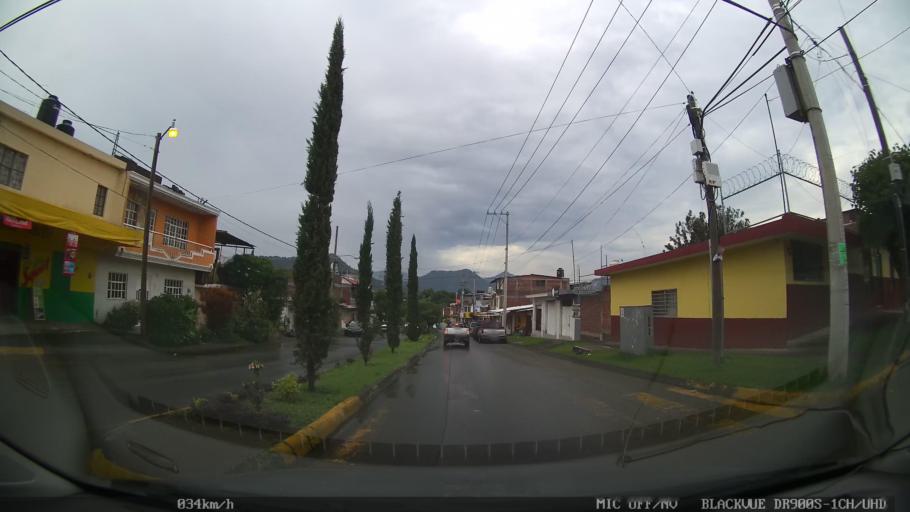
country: MX
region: Michoacan
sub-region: Uruapan
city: Santa Rosa (Santa Barbara)
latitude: 19.3885
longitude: -102.0532
